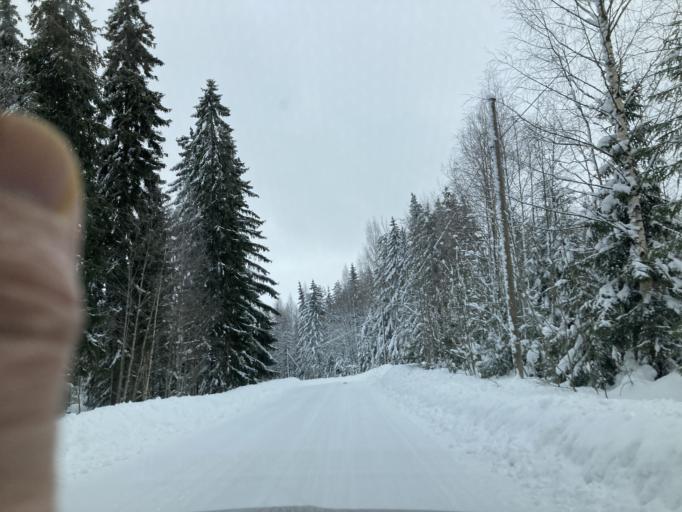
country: FI
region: Central Finland
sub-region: Jaemsae
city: Jaemsae
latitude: 61.8780
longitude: 25.3202
